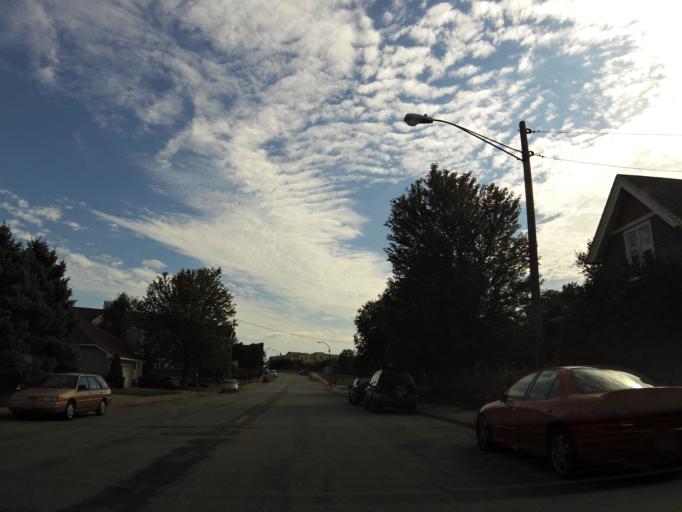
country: US
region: Minnesota
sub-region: Hennepin County
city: Minneapolis
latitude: 44.9941
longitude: -93.2525
